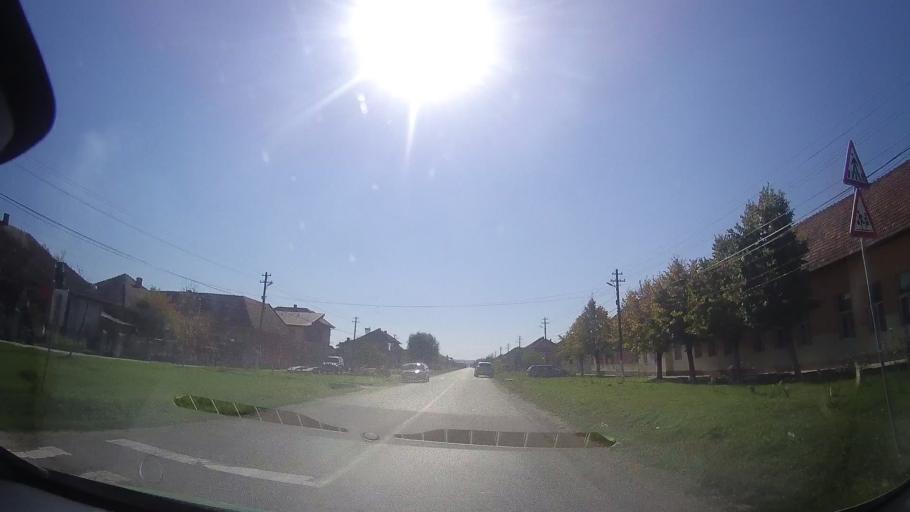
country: RO
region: Timis
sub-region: Comuna Bethausen
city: Bethausen
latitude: 45.8365
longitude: 21.9596
